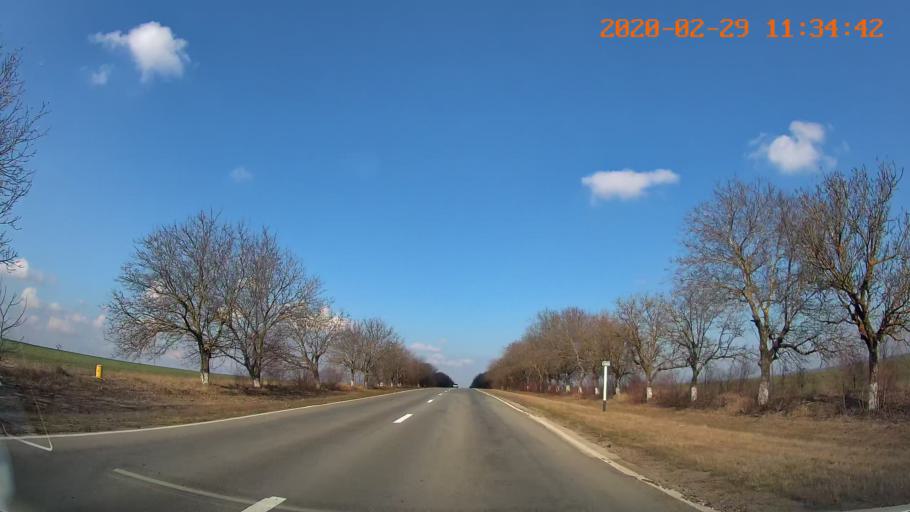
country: MD
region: Rezina
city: Saharna
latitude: 47.5697
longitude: 29.0708
